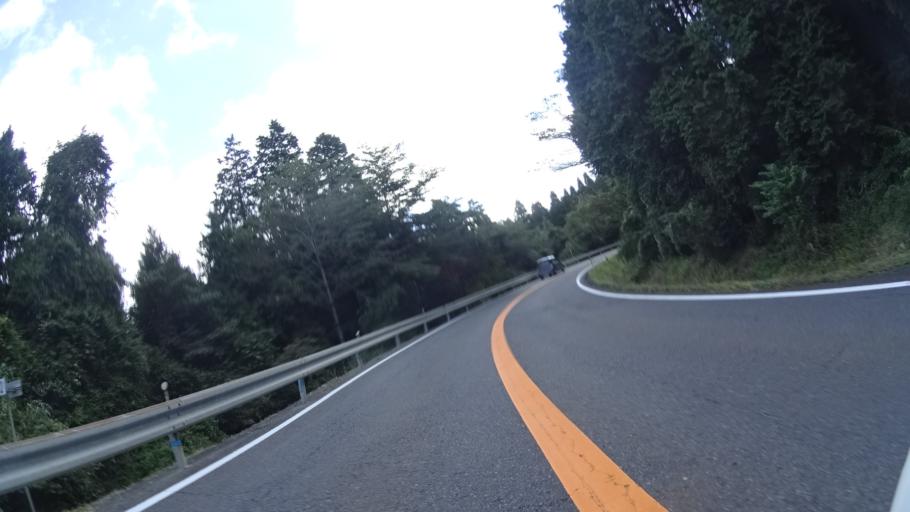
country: JP
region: Oita
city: Tsukawaki
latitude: 33.2344
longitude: 131.2892
